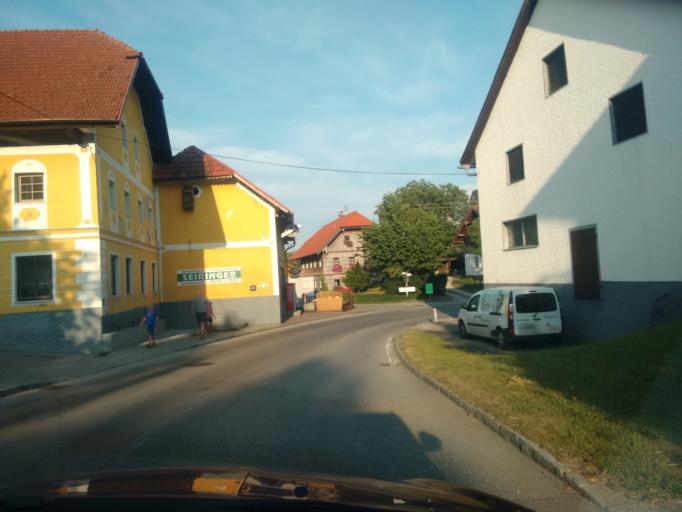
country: AT
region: Upper Austria
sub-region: Politischer Bezirk Vocklabruck
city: Wolfsegg am Hausruck
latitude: 48.1447
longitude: 13.7026
